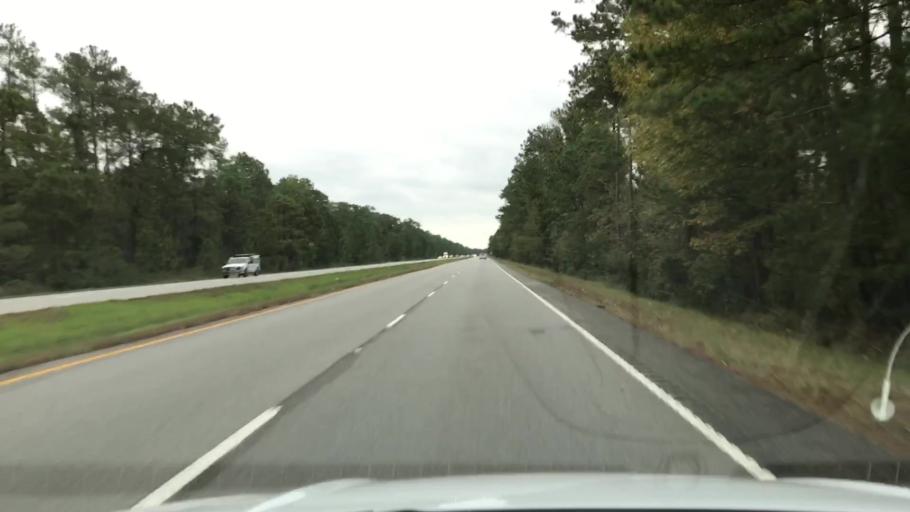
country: US
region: South Carolina
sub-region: Georgetown County
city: Georgetown
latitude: 33.4062
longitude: -79.1968
